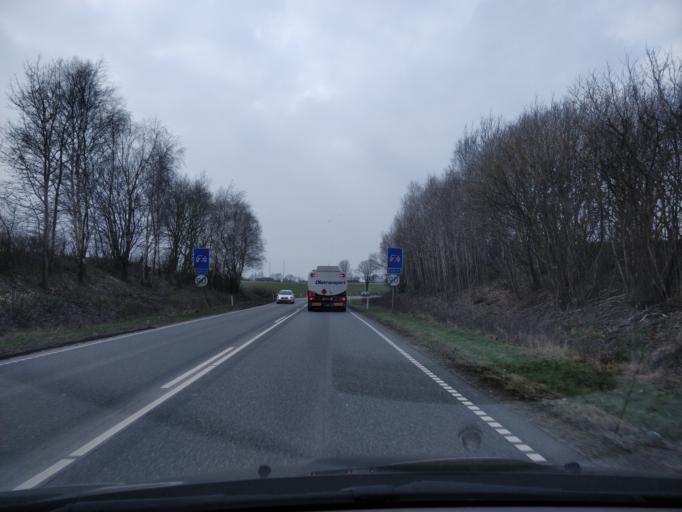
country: DK
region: South Denmark
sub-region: Vejle Kommune
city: Borkop
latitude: 55.6690
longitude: 9.5902
